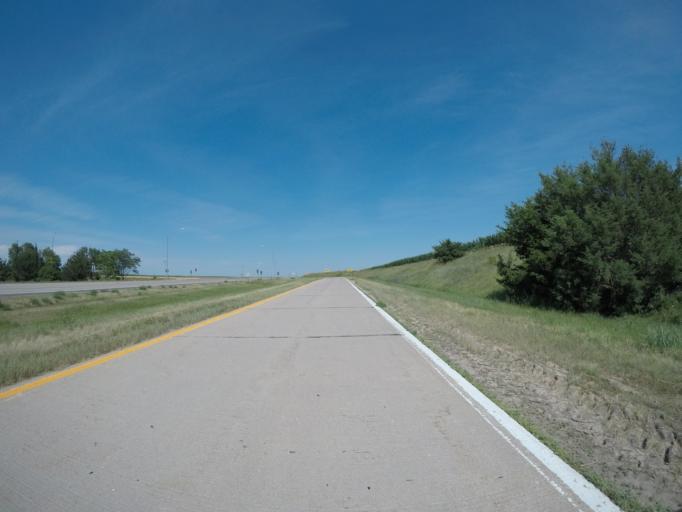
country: US
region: Nebraska
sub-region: Adams County
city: Hastings
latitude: 40.4364
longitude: -98.4347
